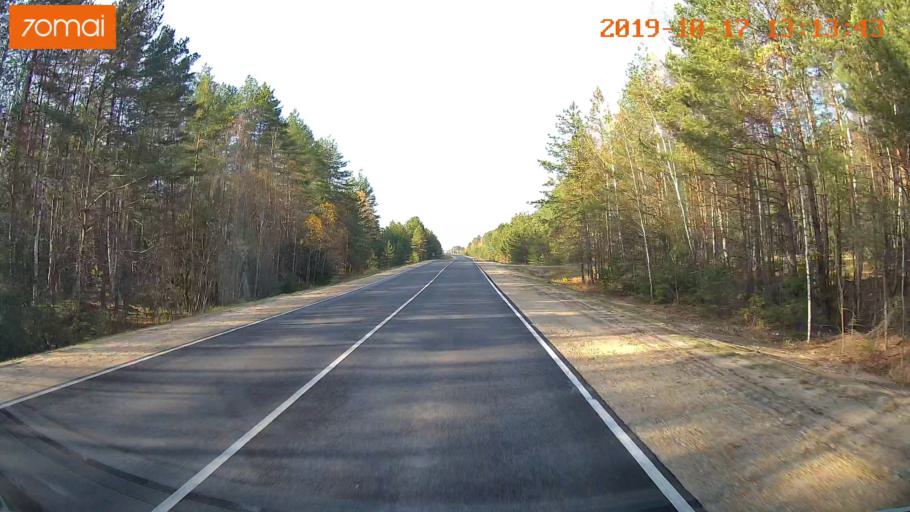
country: RU
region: Rjazan
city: Gus'-Zheleznyy
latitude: 55.0472
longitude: 41.1854
